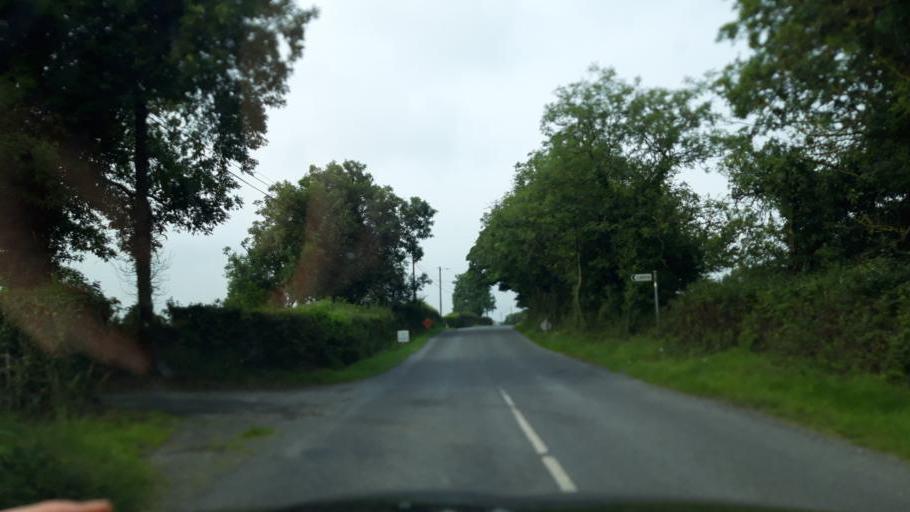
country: IE
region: Munster
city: Fethard
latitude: 52.5814
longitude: -7.6201
